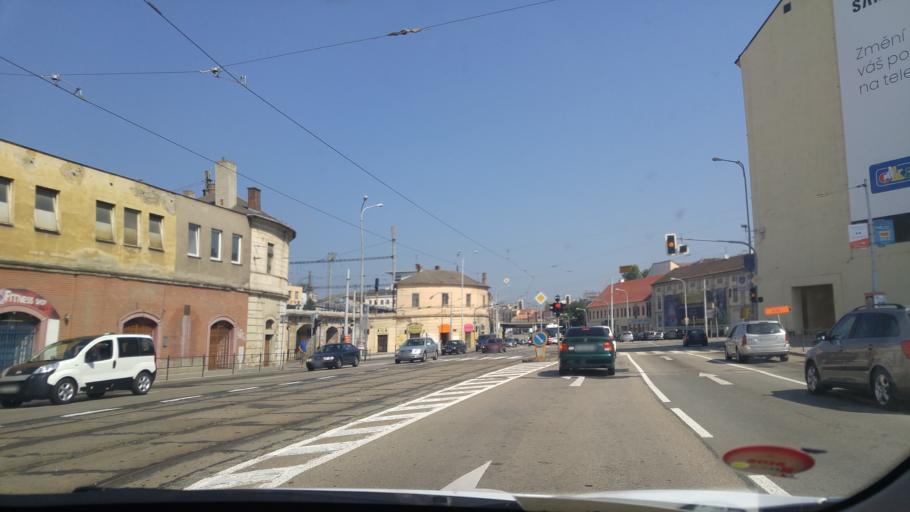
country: CZ
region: South Moravian
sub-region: Mesto Brno
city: Brno
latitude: 49.1910
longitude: 16.6147
